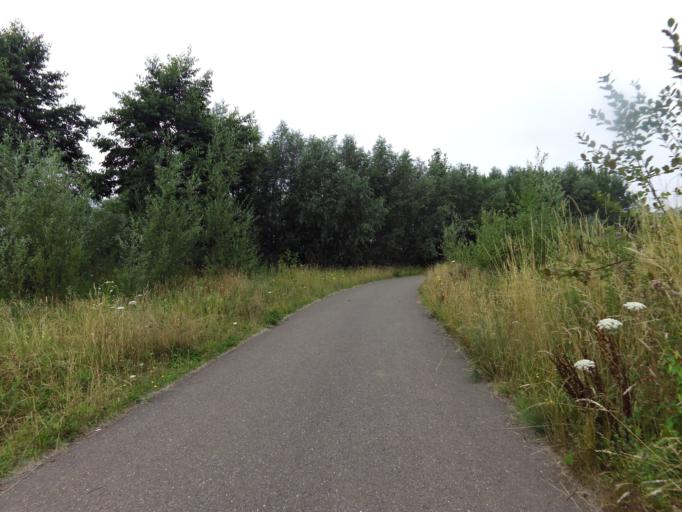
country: NL
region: Limburg
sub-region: Gemeente Heerlen
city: Heerlen
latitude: 50.8853
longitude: 5.9657
